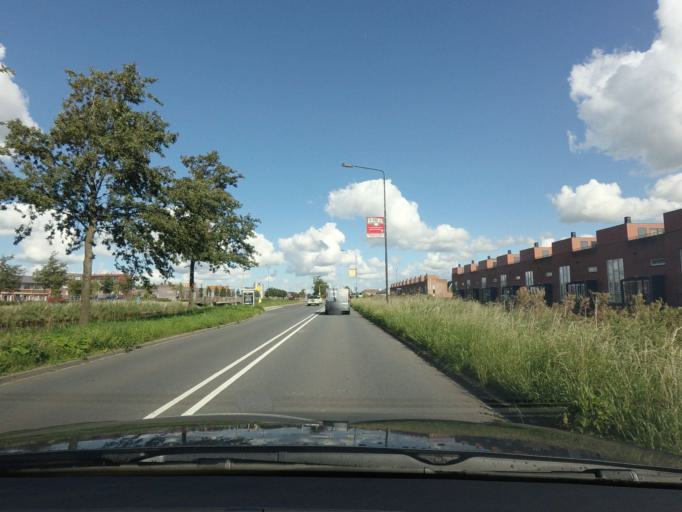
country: NL
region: North Holland
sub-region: Gemeente Langedijk
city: Broek op Langedijk
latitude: 52.6454
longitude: 4.8185
